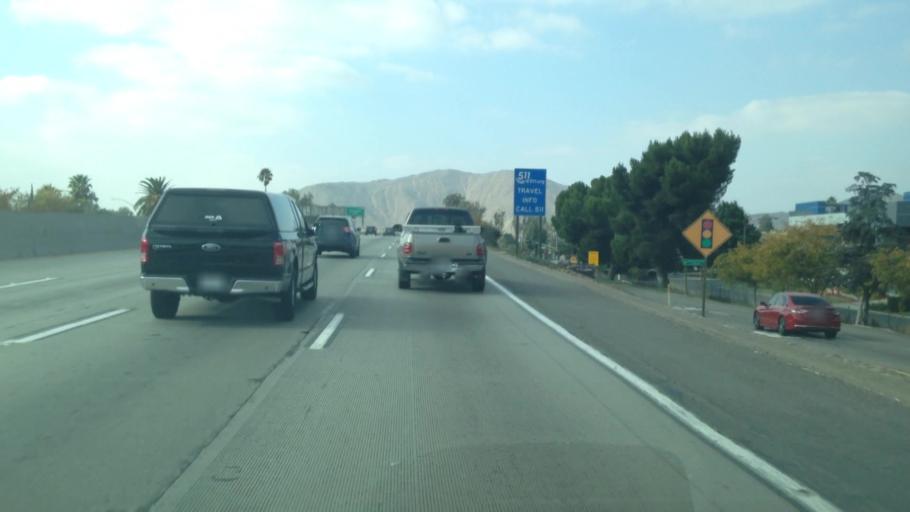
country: US
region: California
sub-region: Riverside County
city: Rubidoux
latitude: 33.9999
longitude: -117.3729
